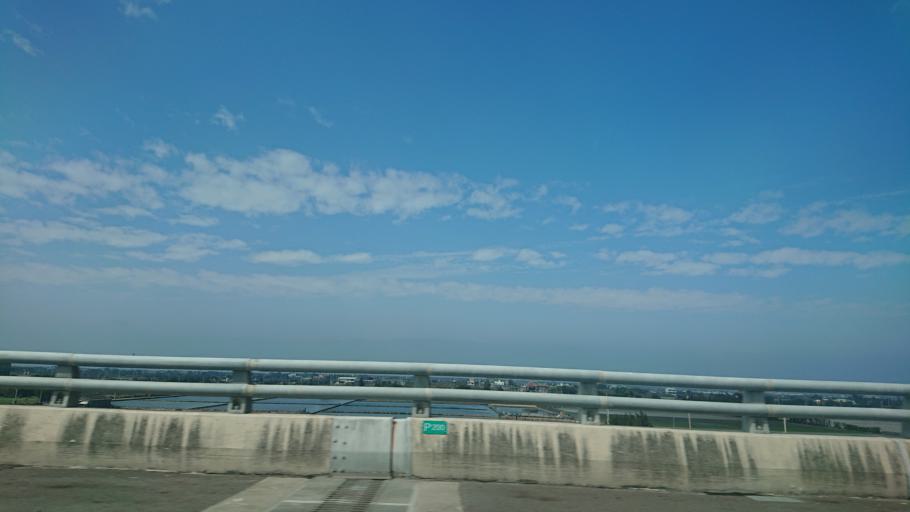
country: TW
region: Taiwan
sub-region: Yunlin
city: Douliu
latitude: 23.8452
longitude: 120.2936
